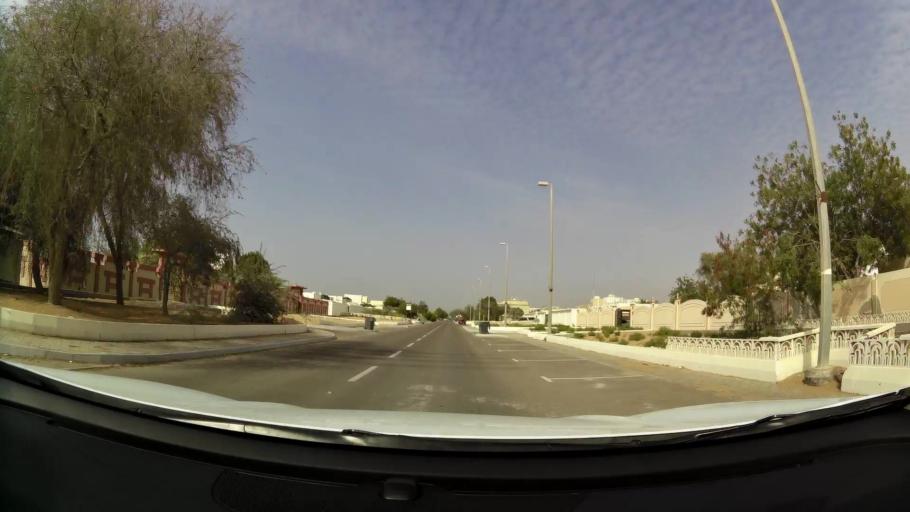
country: AE
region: Abu Dhabi
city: Abu Dhabi
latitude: 24.6020
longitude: 54.7022
